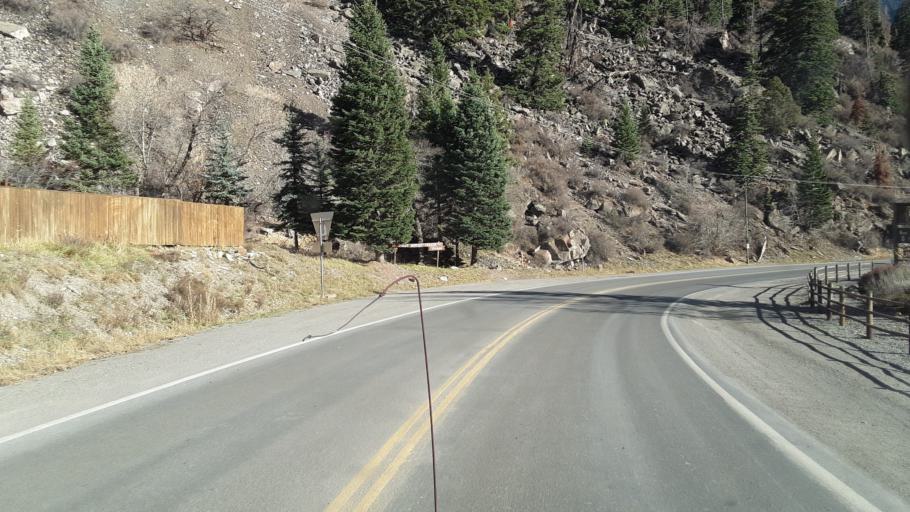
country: US
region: Colorado
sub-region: Ouray County
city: Ouray
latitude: 38.0296
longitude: -107.6723
